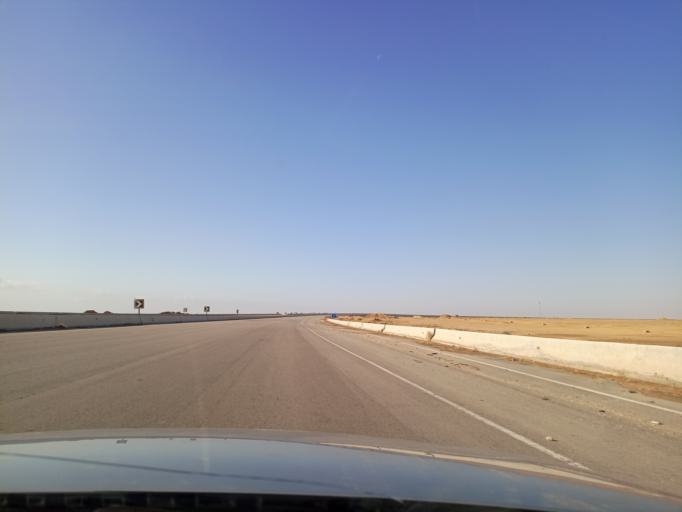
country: EG
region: Muhafazat al Fayyum
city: Tamiyah
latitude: 29.5696
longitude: 30.8368
